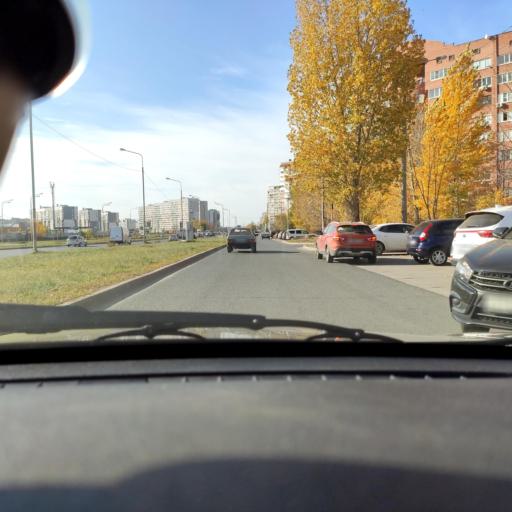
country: RU
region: Samara
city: Tol'yatti
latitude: 53.5348
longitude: 49.3486
